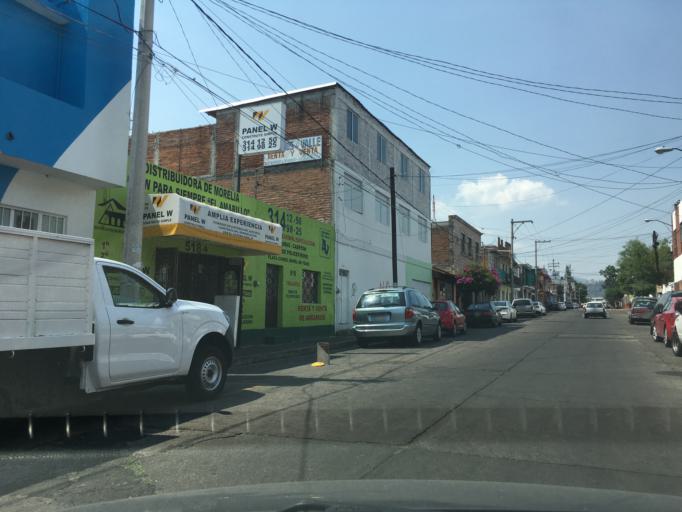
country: MX
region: Michoacan
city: Morelia
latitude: 19.7026
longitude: -101.1728
